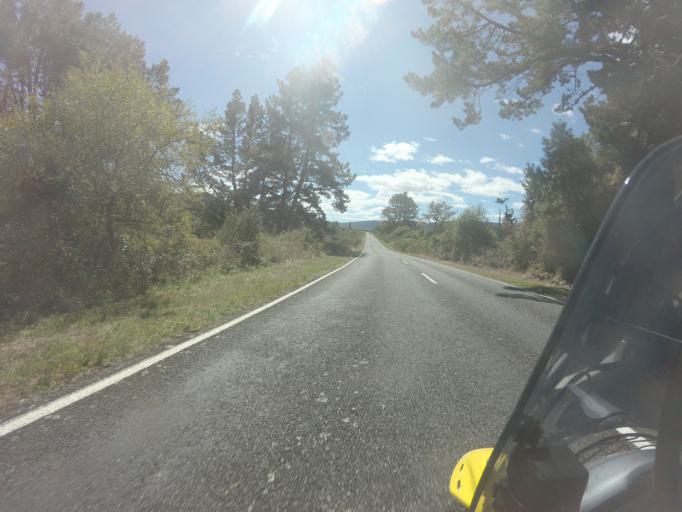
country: NZ
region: Bay of Plenty
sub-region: Kawerau District
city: Kawerau
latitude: -38.2490
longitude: 176.8254
